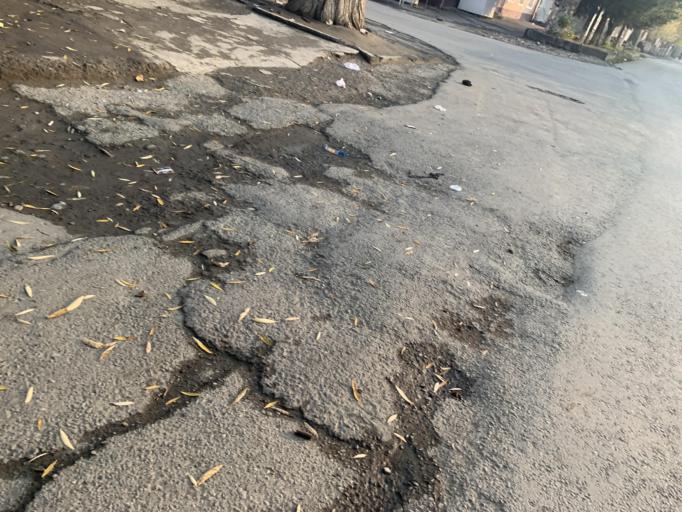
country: UZ
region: Fergana
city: Qo`qon
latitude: 40.5226
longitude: 70.9385
